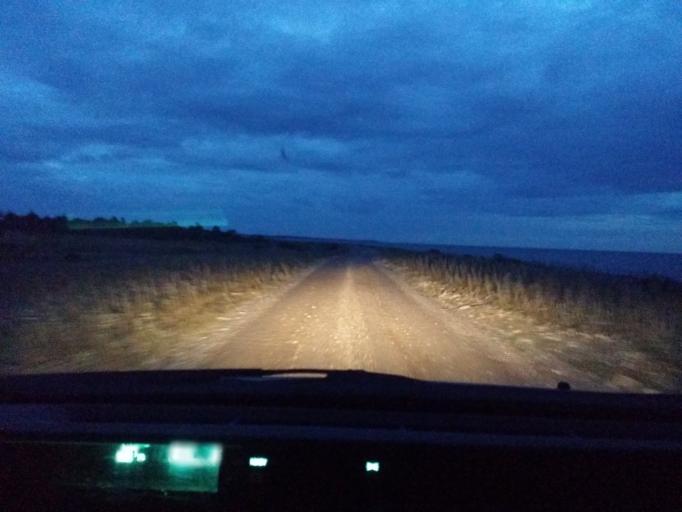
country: SE
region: Kalmar
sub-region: Borgholms Kommun
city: Borgholm
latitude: 57.1347
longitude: 16.9029
